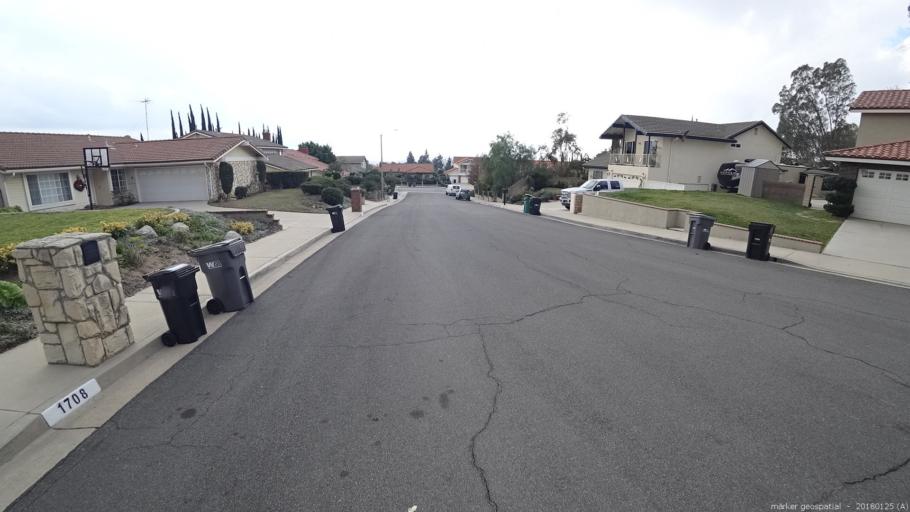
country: US
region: California
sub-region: Los Angeles County
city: Walnut
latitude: 33.9915
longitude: -117.8330
